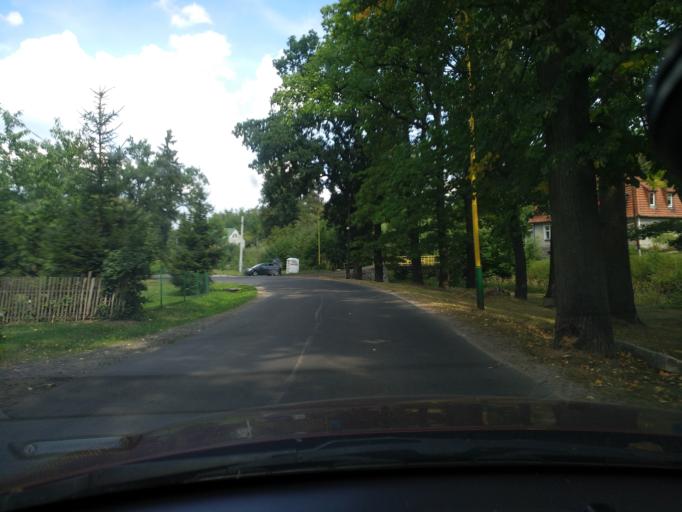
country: PL
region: Lower Silesian Voivodeship
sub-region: Powiat jeleniogorski
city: Stara Kamienica
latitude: 50.9139
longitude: 15.5733
